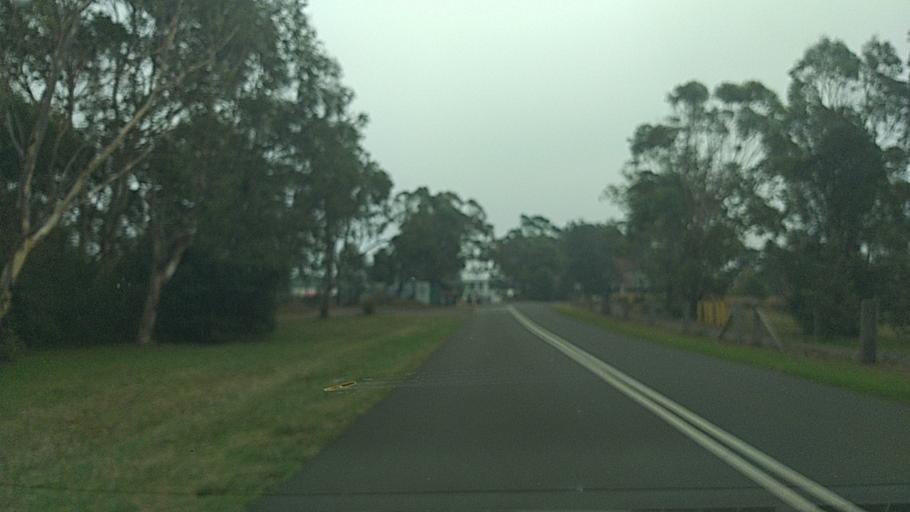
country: AU
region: New South Wales
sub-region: Shellharbour
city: Flinders
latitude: -34.6016
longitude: 150.8604
